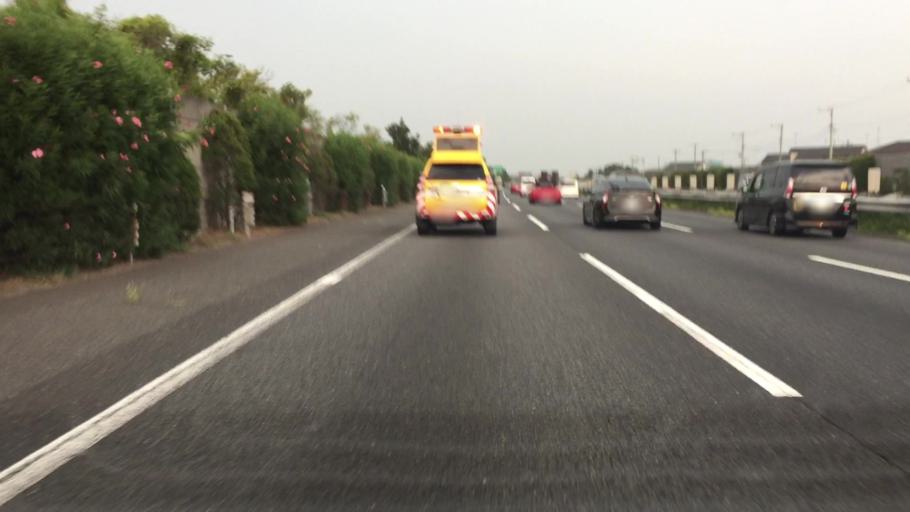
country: JP
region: Saitama
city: Kazo
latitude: 36.1341
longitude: 139.6195
